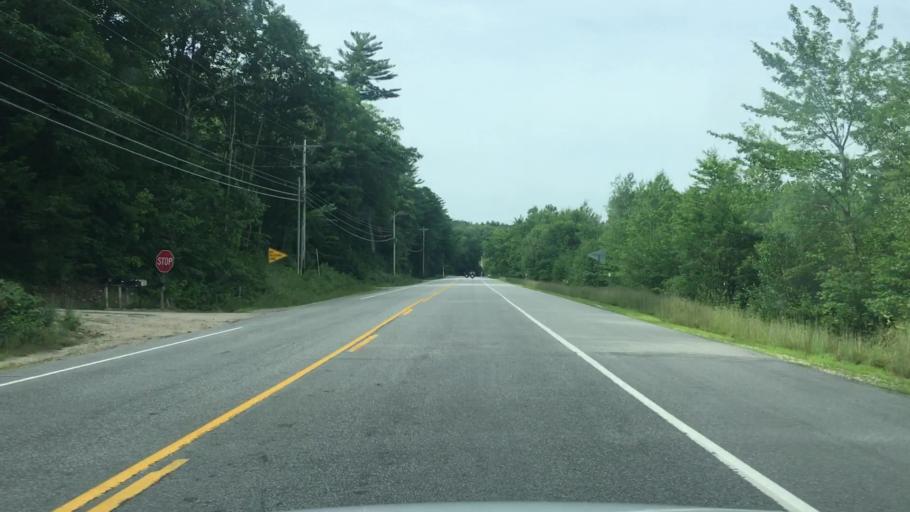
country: US
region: New Hampshire
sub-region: Carroll County
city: Sandwich
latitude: 43.8049
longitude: -71.3561
